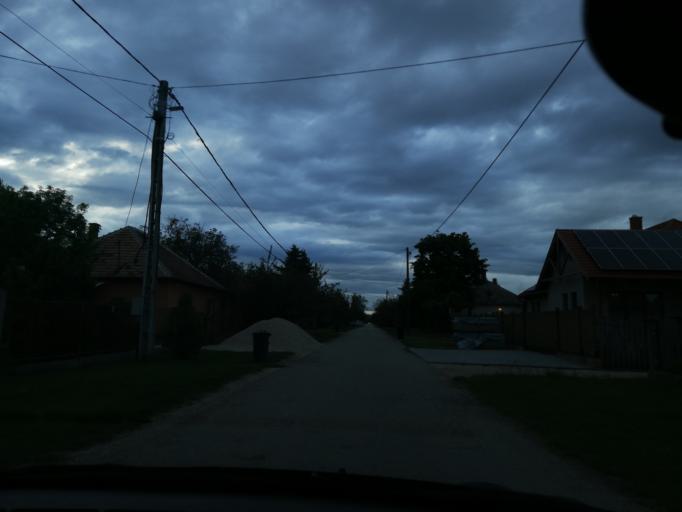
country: HU
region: Fejer
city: Pakozd
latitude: 47.1699
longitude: 18.5731
